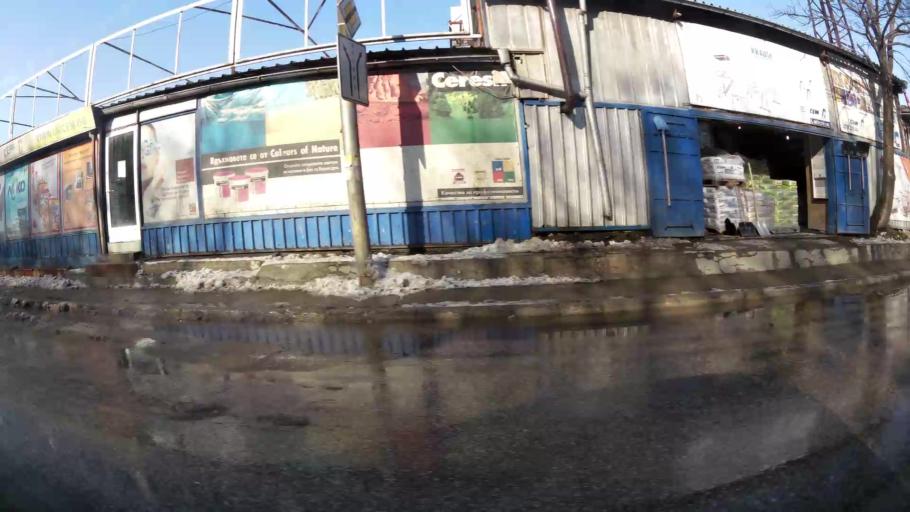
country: BG
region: Sofia-Capital
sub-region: Stolichna Obshtina
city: Sofia
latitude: 42.6668
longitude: 23.3394
